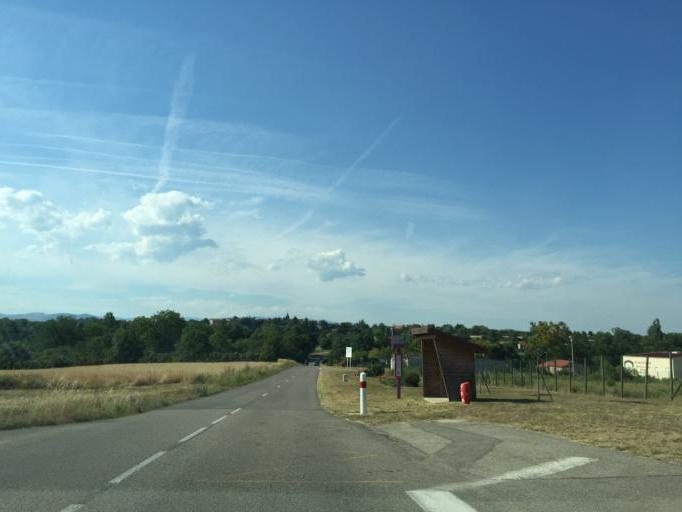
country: FR
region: Rhone-Alpes
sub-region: Departement de l'Ardeche
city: Quintenas
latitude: 45.1801
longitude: 4.6919
